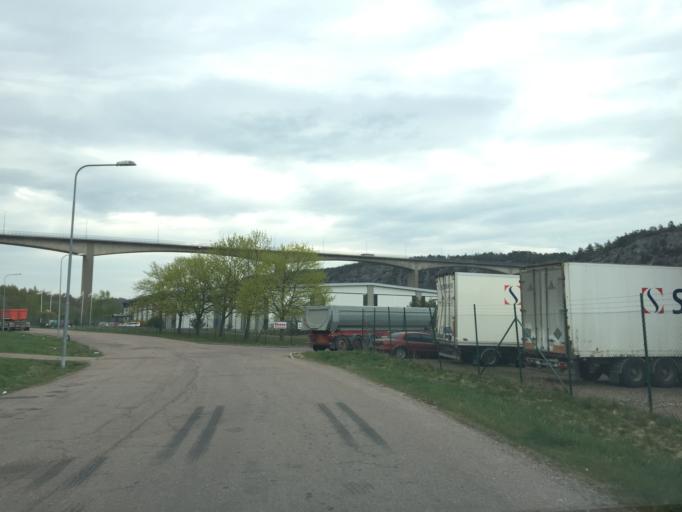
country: SE
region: Vaestra Goetaland
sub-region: Goteborg
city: Gardsten
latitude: 57.7964
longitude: 12.0089
